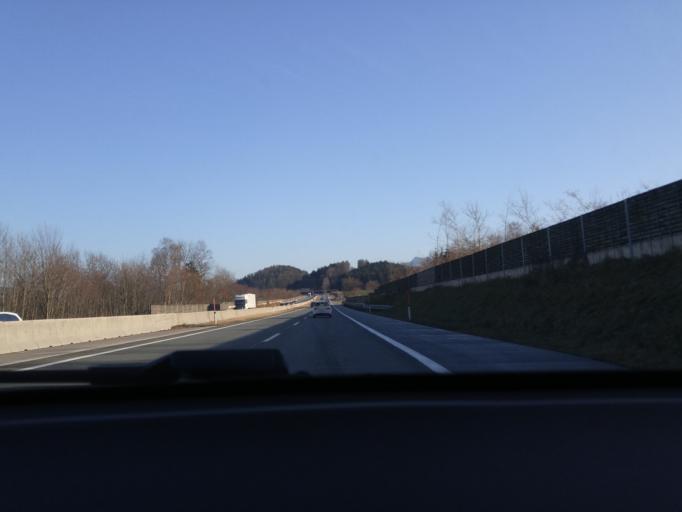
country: AT
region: Salzburg
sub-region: Politischer Bezirk Salzburg-Umgebung
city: Plainfeld
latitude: 47.8522
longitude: 13.1693
